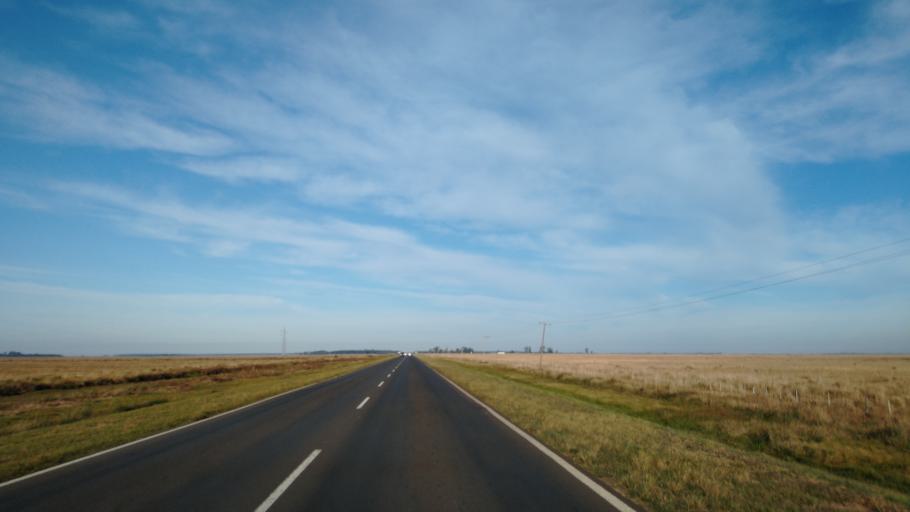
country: AR
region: Corrientes
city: La Cruz
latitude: -29.2213
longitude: -56.7118
